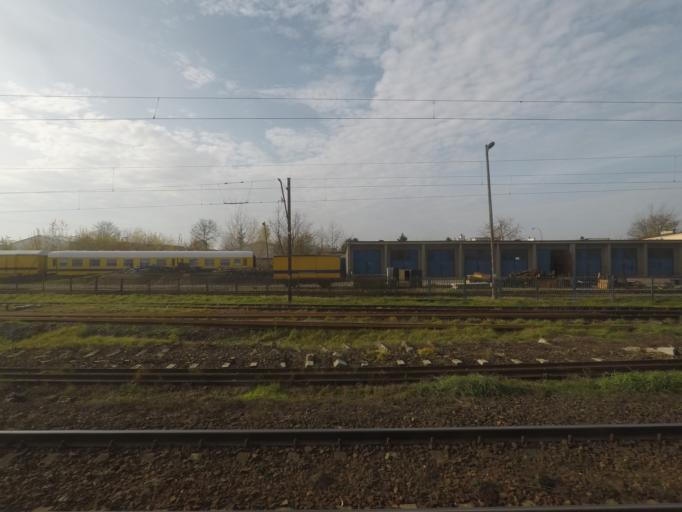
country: PL
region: Subcarpathian Voivodeship
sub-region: Rzeszow
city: Rzeszow
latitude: 50.0528
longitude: 21.9940
